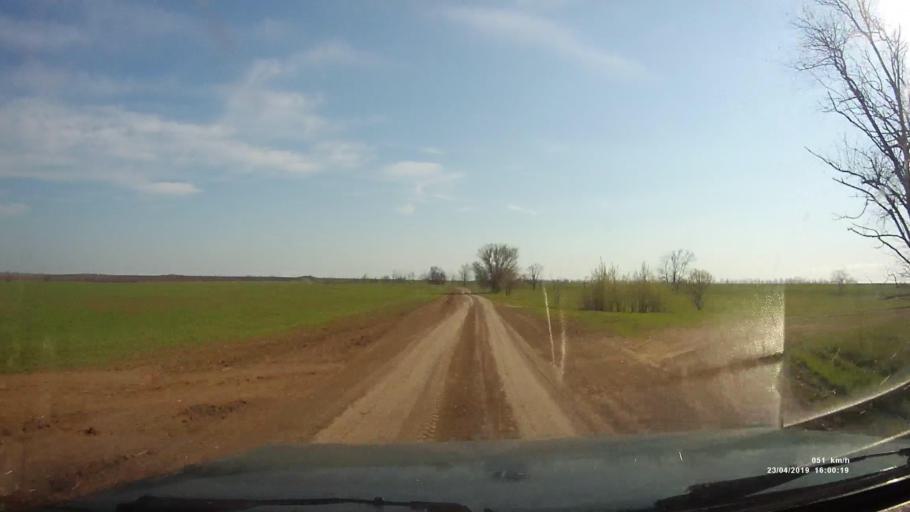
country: RU
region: Rostov
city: Remontnoye
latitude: 46.5102
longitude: 43.1078
